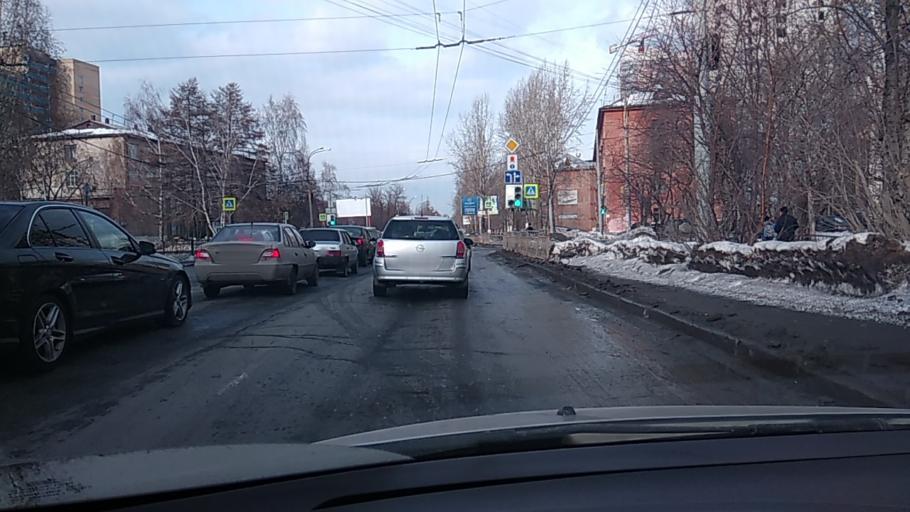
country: RU
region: Sverdlovsk
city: Yekaterinburg
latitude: 56.8603
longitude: 60.6535
